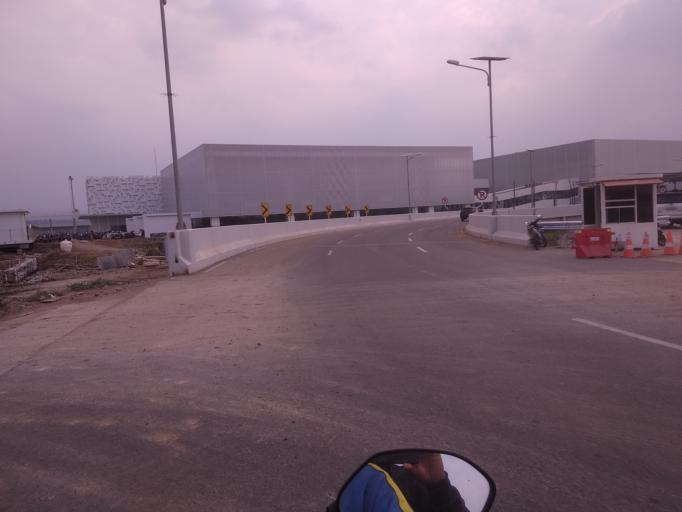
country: ID
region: Central Java
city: Semarang
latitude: -6.9665
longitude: 110.3770
